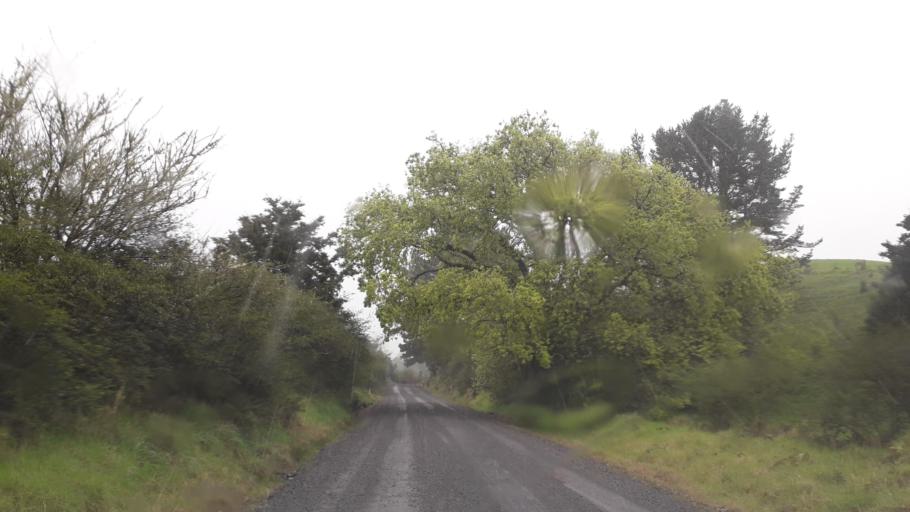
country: NZ
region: Northland
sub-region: Far North District
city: Waimate North
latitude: -35.4874
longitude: 173.7009
